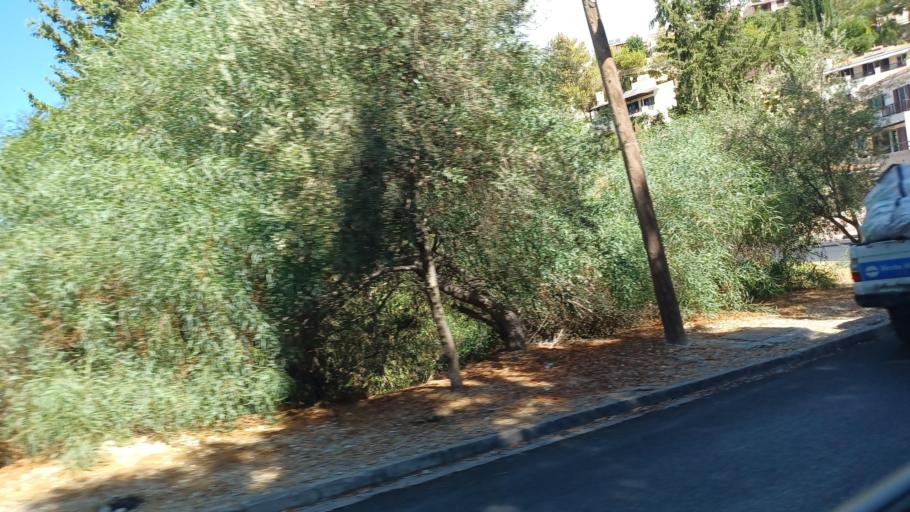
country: CY
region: Pafos
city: Tala
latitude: 34.8474
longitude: 32.4327
